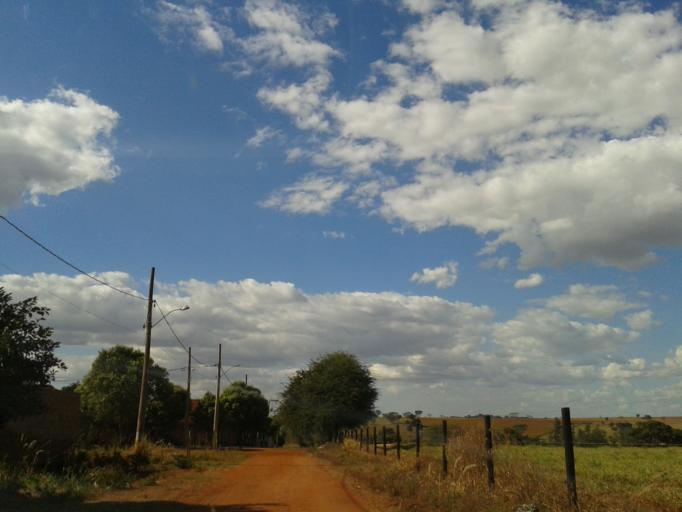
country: BR
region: Minas Gerais
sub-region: Capinopolis
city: Capinopolis
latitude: -18.6959
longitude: -49.5653
